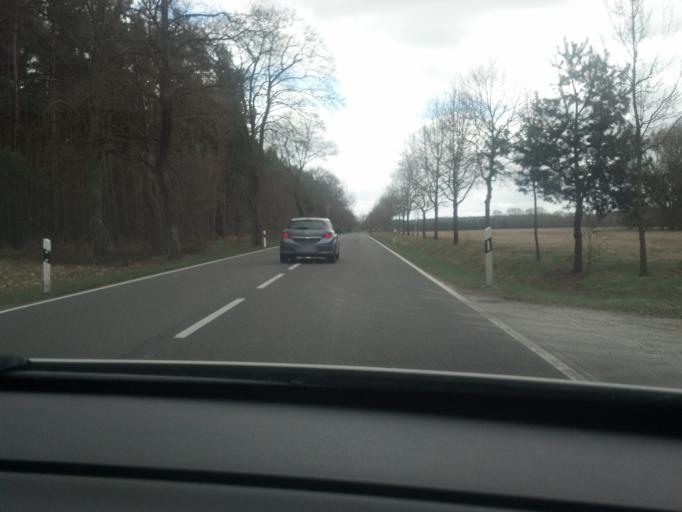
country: DE
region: Mecklenburg-Vorpommern
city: Rechlin
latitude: 53.2967
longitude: 12.7828
